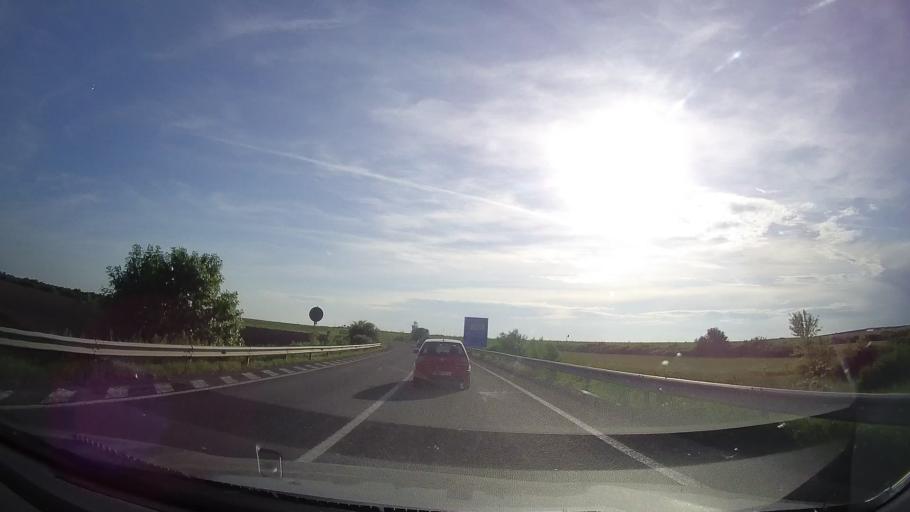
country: RO
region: Timis
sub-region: Oras Recas
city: Izvin
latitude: 45.7975
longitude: 21.4219
